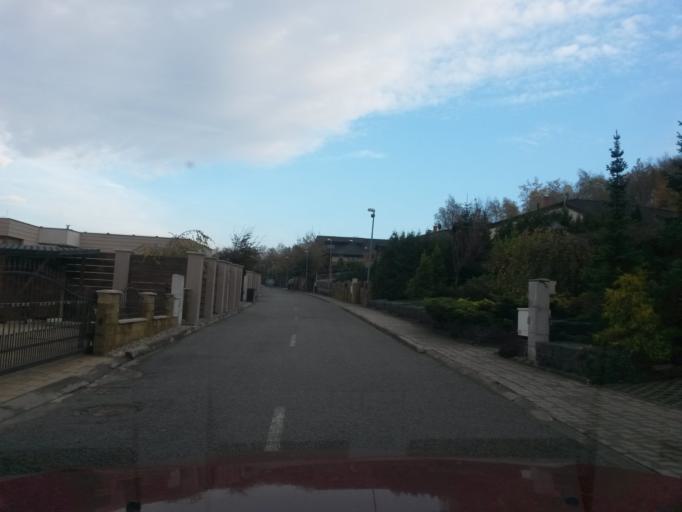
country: SK
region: Kosicky
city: Kosice
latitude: 48.7703
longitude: 21.2143
